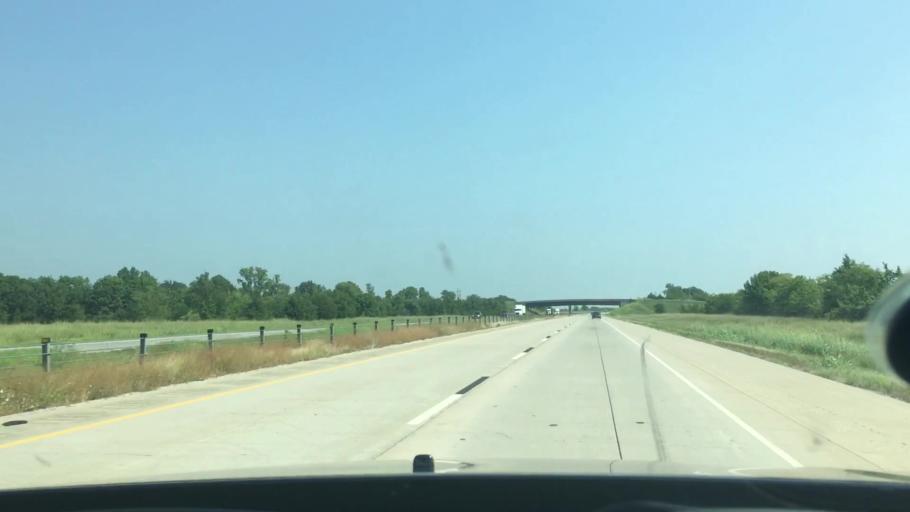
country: US
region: Oklahoma
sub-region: Bryan County
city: Durant
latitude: 34.0735
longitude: -96.3409
